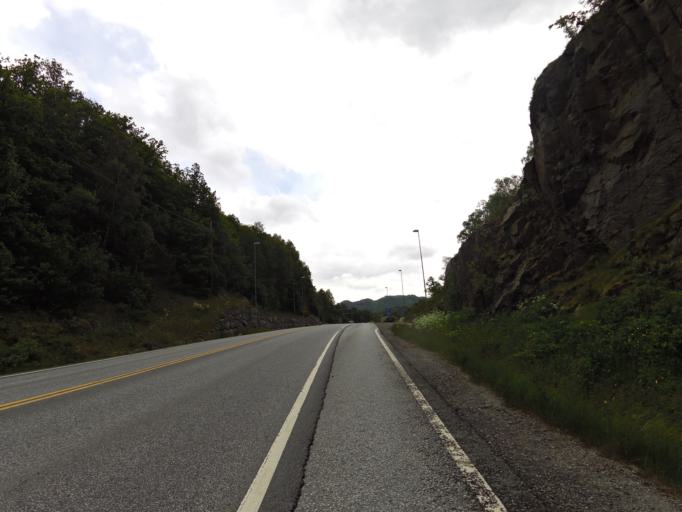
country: NO
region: Vest-Agder
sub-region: Lyngdal
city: Lyngdal
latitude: 58.1121
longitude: 6.9392
